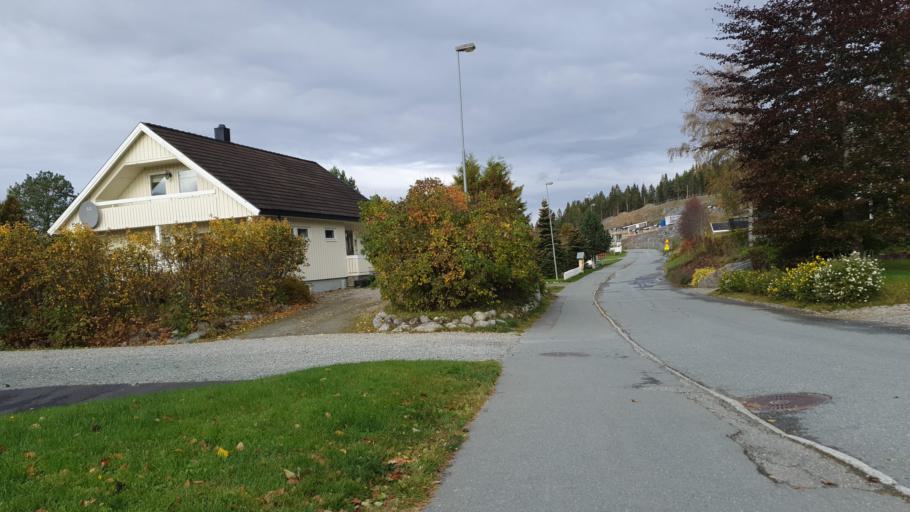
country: NO
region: Sor-Trondelag
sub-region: Klaebu
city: Klaebu
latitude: 63.2983
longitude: 10.4651
